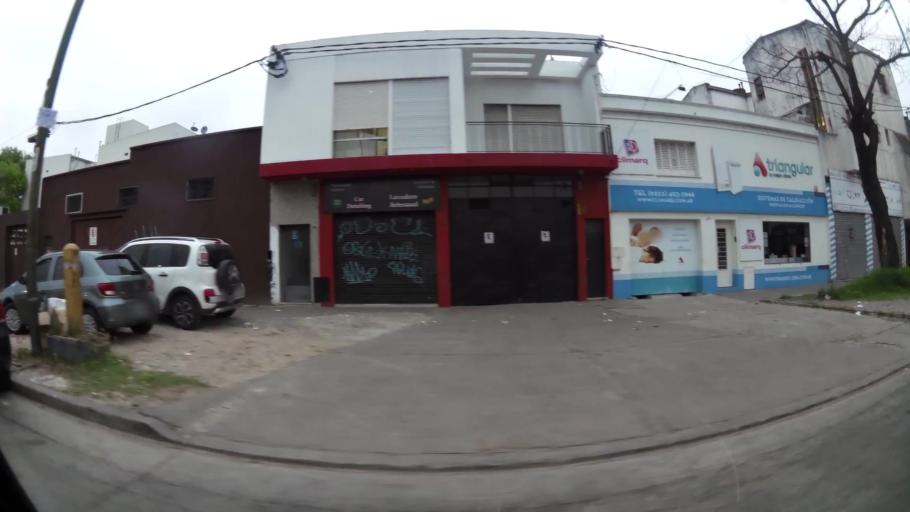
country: AR
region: Buenos Aires
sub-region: Partido de La Plata
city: La Plata
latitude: -34.9065
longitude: -57.9754
